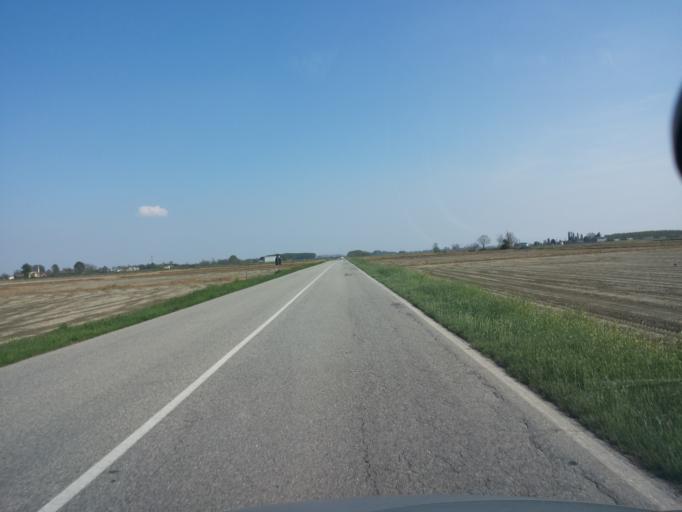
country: IT
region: Lombardy
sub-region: Provincia di Pavia
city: Candia Lomellina
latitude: 45.1945
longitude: 8.5913
